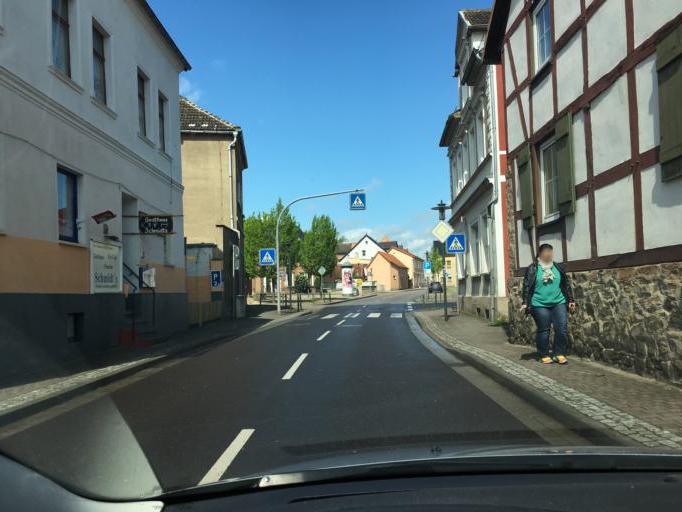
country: DE
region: Saxony-Anhalt
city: Haldensleben I
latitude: 52.2652
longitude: 11.4219
